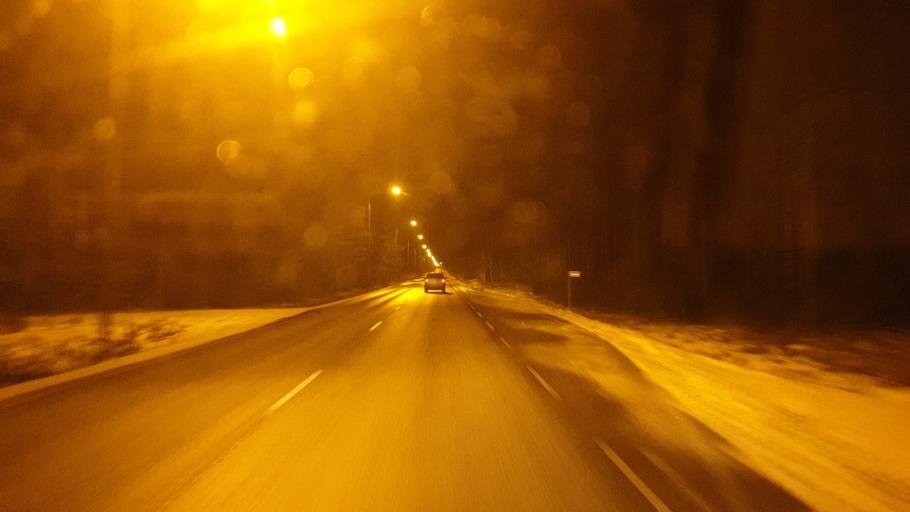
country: FI
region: Northern Savo
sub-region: Sisae-Savo
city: Suonenjoki
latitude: 62.6653
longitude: 27.3594
